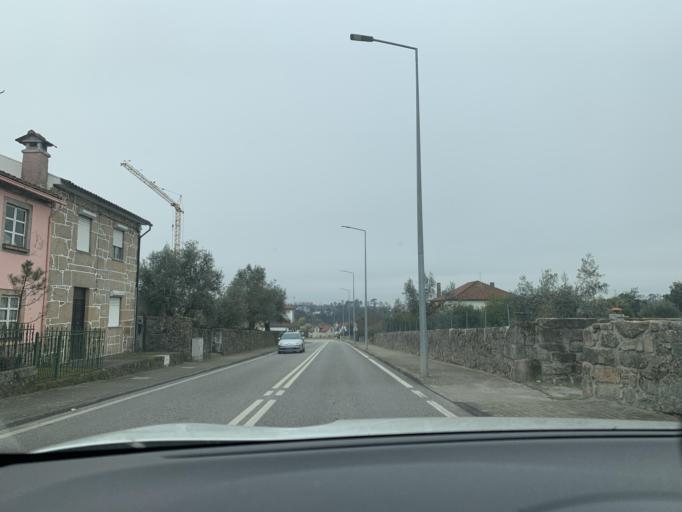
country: PT
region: Viseu
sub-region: Concelho de Tondela
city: Tondela
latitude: 40.5253
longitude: -8.0661
